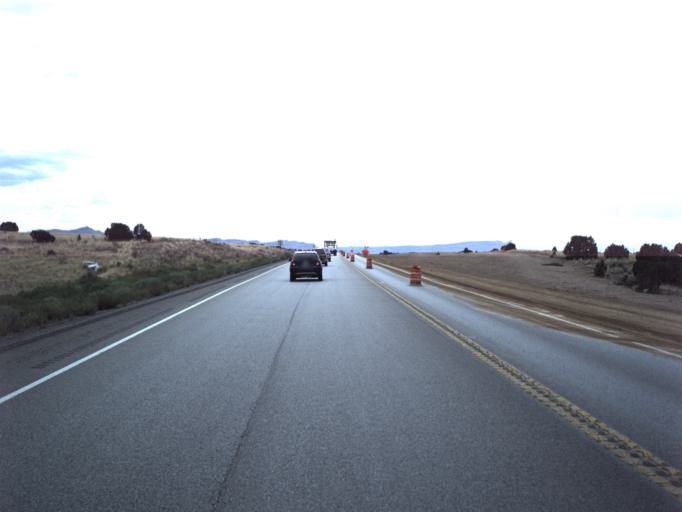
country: US
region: Utah
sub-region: Carbon County
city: East Carbon City
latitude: 39.4172
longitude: -110.4379
